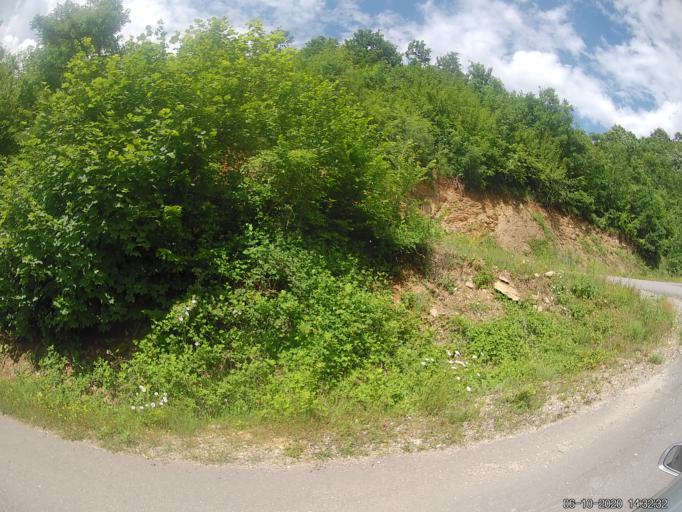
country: XK
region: Prizren
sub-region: Komuna e Therandes
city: Budakovo
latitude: 42.4159
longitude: 20.9253
